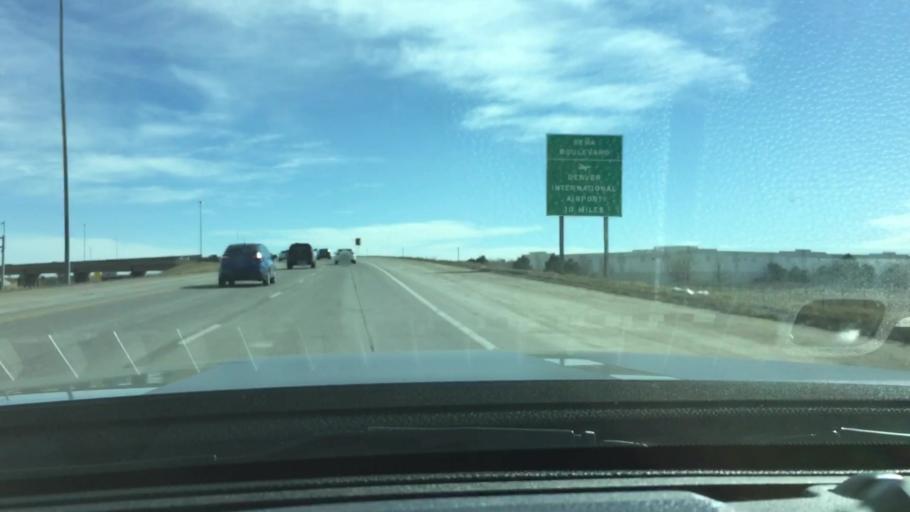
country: US
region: Colorado
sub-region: Adams County
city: Aurora
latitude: 39.7682
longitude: -104.8003
